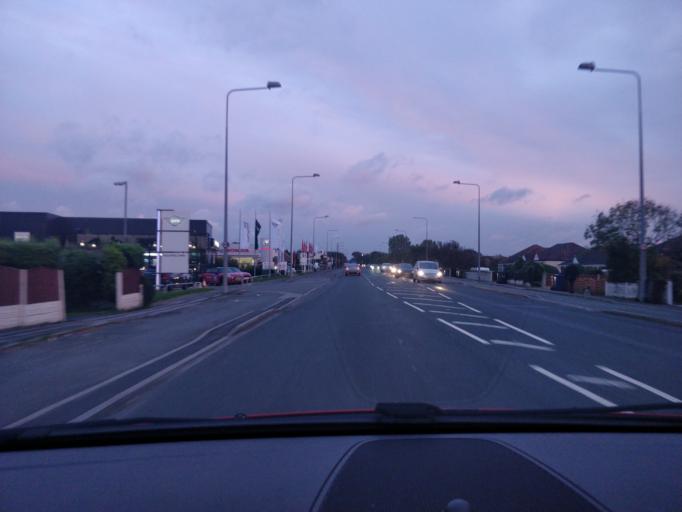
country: GB
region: England
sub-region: Sefton
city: Southport
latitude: 53.6291
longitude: -2.9660
